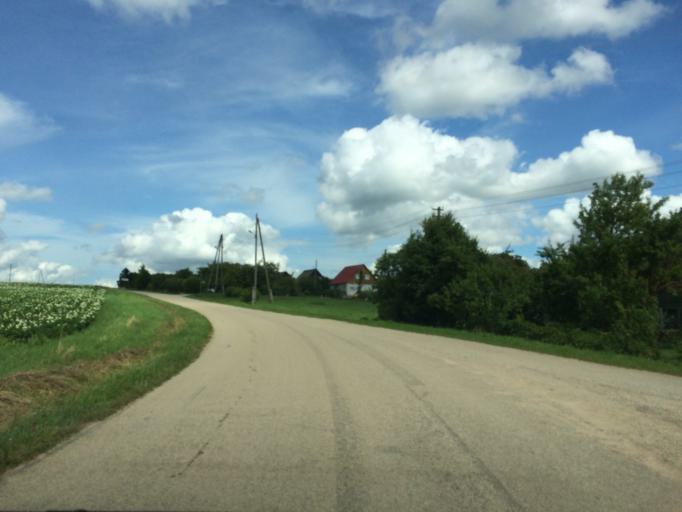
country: LV
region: Ludzas Rajons
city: Ludza
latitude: 56.6327
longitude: 27.5202
